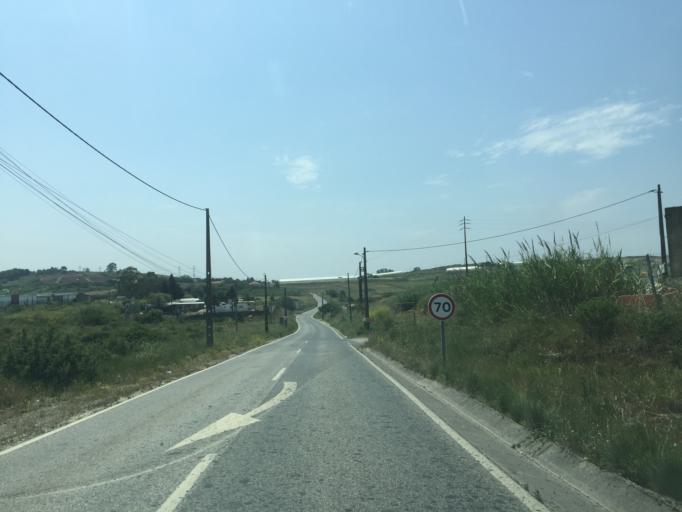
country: PT
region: Lisbon
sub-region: Mafra
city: Venda do Pinheiro
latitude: 38.8879
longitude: -9.1882
